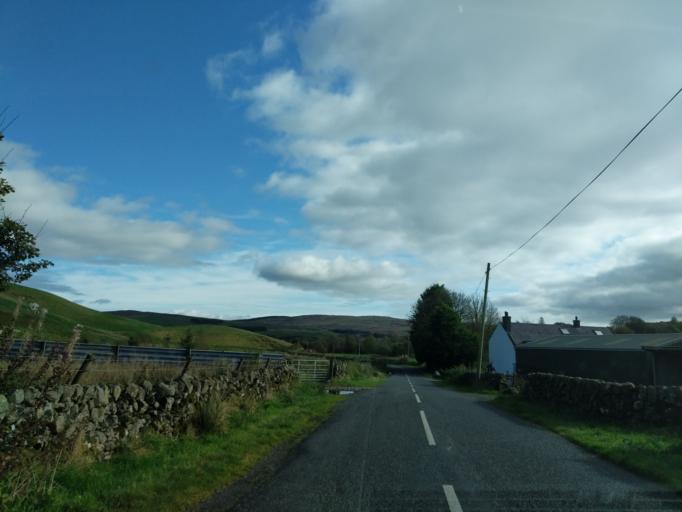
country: GB
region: Scotland
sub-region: Dumfries and Galloway
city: Sanquhar
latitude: 55.1619
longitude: -3.9867
